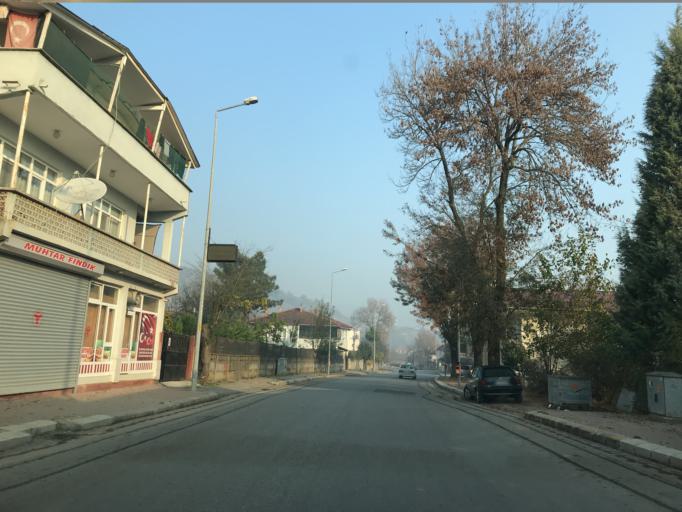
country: TR
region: Duzce
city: Cumayeri
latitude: 40.8821
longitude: 30.9513
